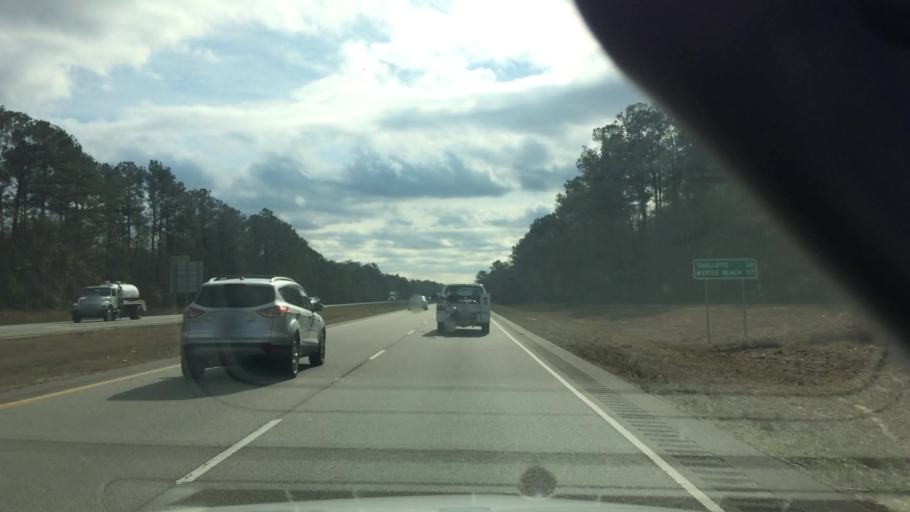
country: US
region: North Carolina
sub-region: Brunswick County
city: Leland
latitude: 34.1700
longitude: -78.0885
